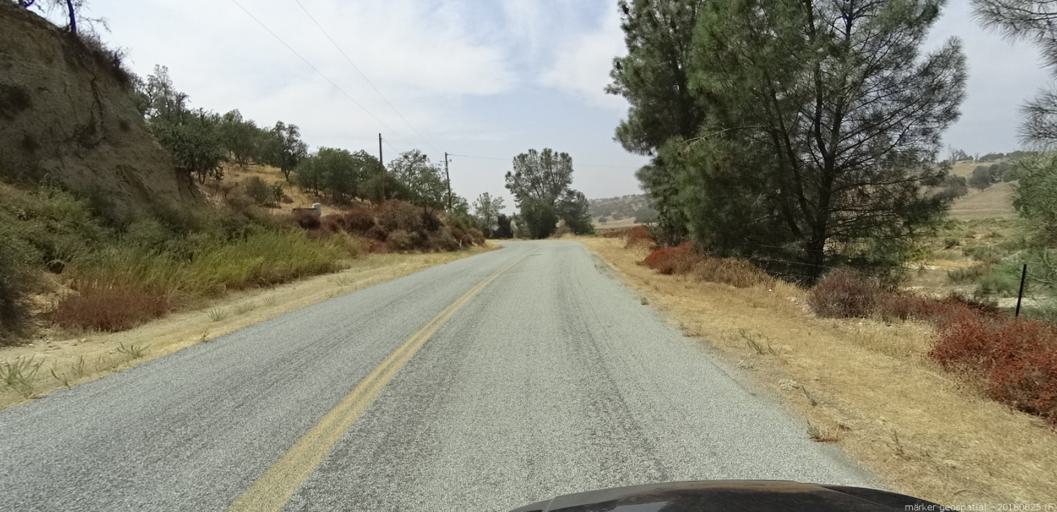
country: US
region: California
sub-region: San Luis Obispo County
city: San Miguel
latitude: 35.8350
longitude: -120.6307
